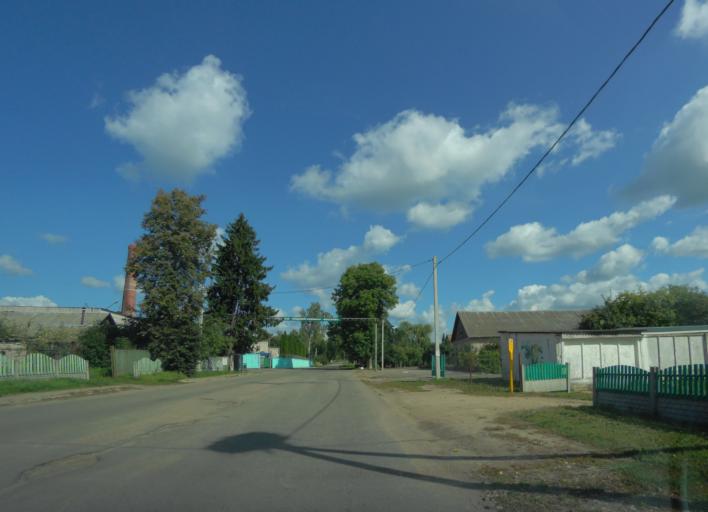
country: BY
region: Minsk
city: Zyembin
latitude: 54.3621
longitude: 28.3428
